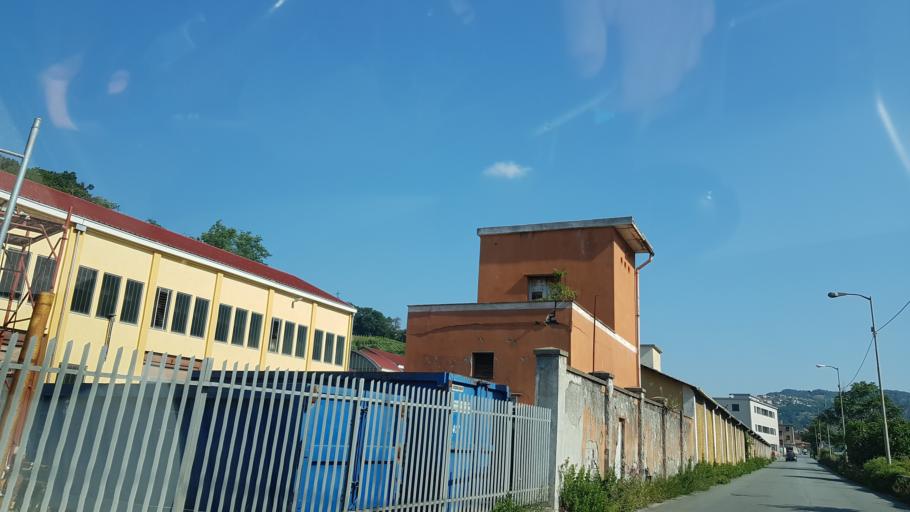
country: IT
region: Liguria
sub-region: Provincia di Genova
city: Manesseno
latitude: 44.4833
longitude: 8.9212
